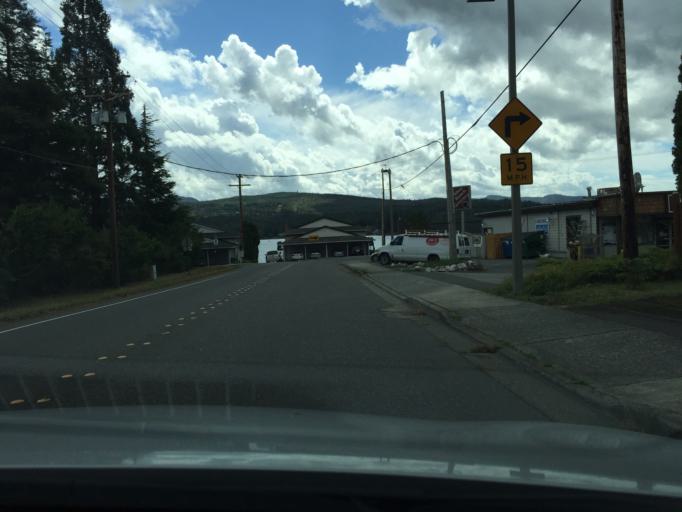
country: US
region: Washington
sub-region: Whatcom County
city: Geneva
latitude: 48.7669
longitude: -122.4122
